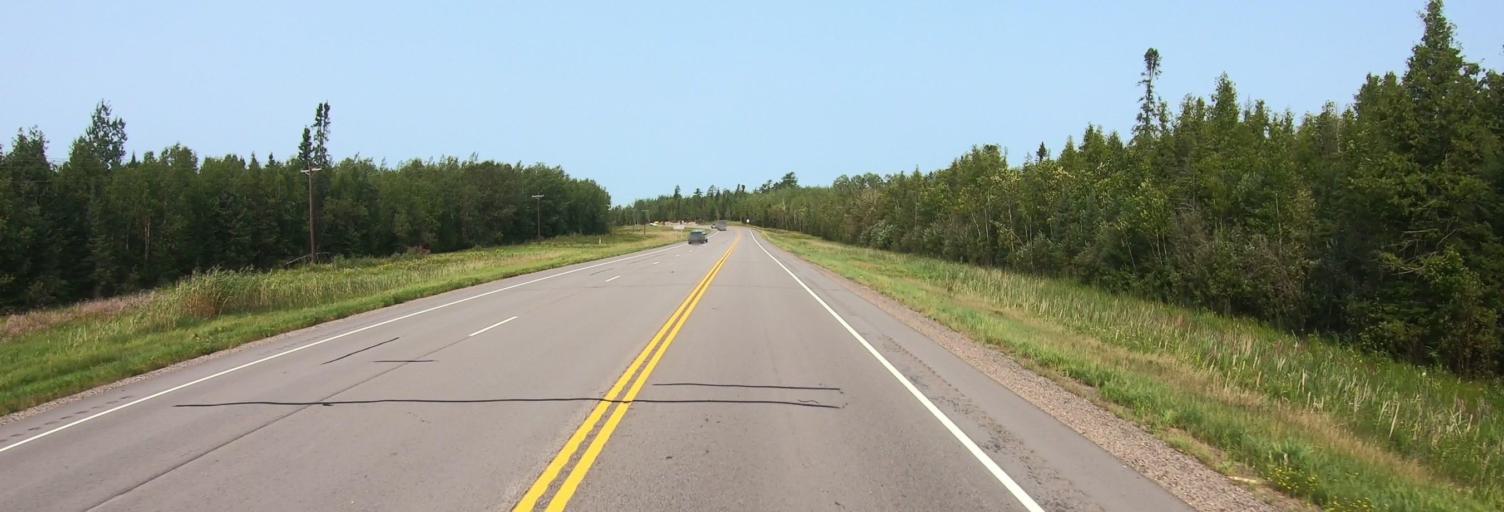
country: CA
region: Ontario
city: Fort Frances
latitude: 48.3987
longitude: -93.0151
